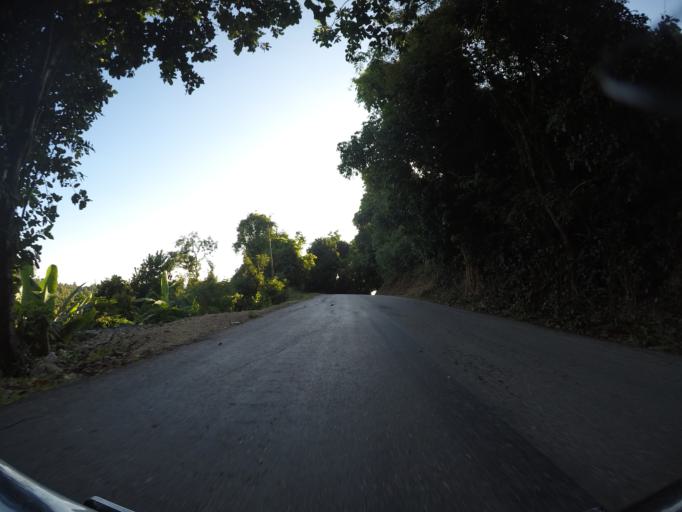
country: TZ
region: Pemba South
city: Mtambile
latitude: -5.3795
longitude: 39.6843
